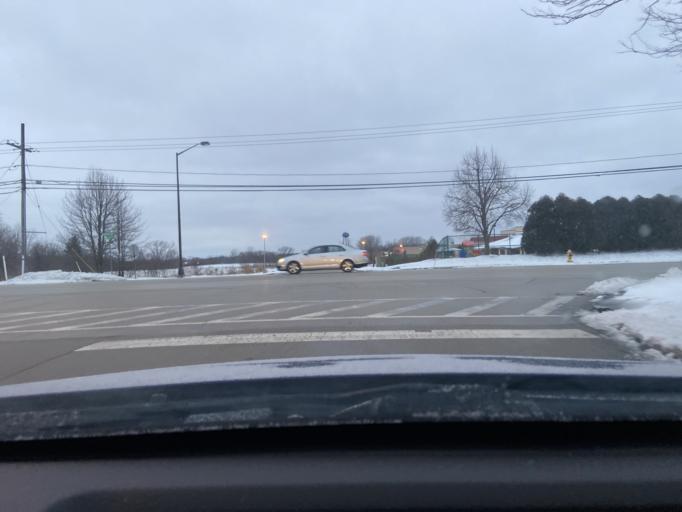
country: US
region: Illinois
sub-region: Lake County
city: Grayslake
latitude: 42.3431
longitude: -88.0239
